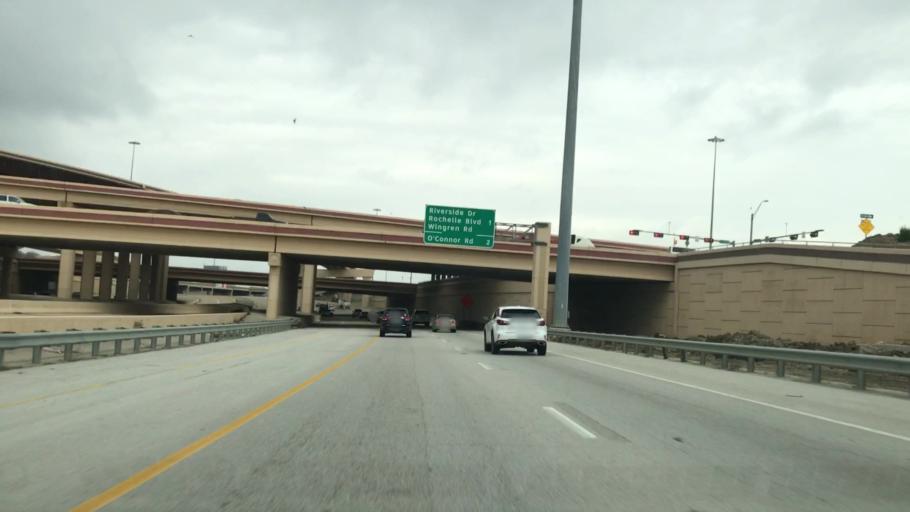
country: US
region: Texas
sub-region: Dallas County
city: Irving
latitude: 32.8450
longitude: -96.9107
